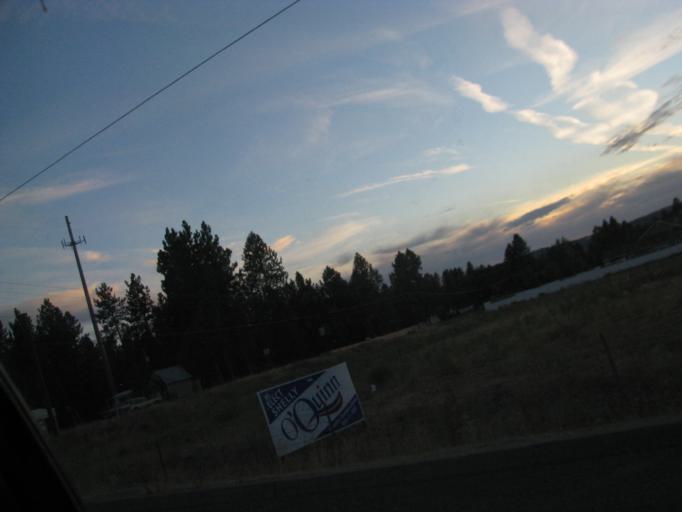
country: US
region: Washington
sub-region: Spokane County
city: Mead
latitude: 47.8023
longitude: -117.3489
